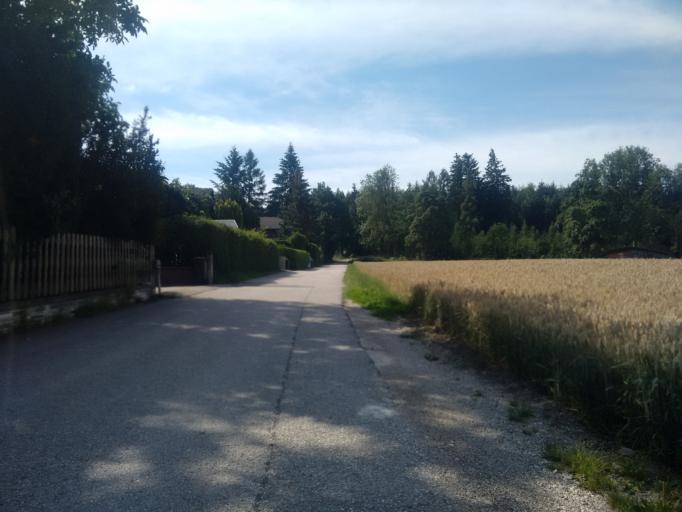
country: AT
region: Upper Austria
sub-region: Wels-Land
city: Gunskirchen
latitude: 48.1904
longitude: 13.9676
